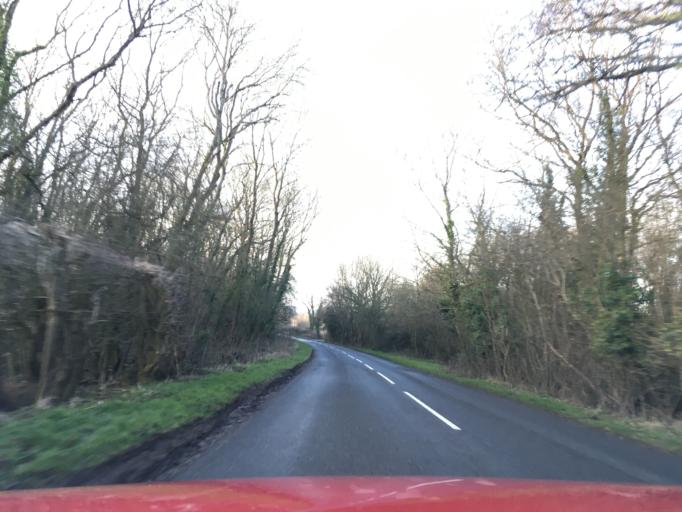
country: GB
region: England
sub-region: Warwickshire
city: Stratford-upon-Avon
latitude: 52.2421
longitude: -1.7220
